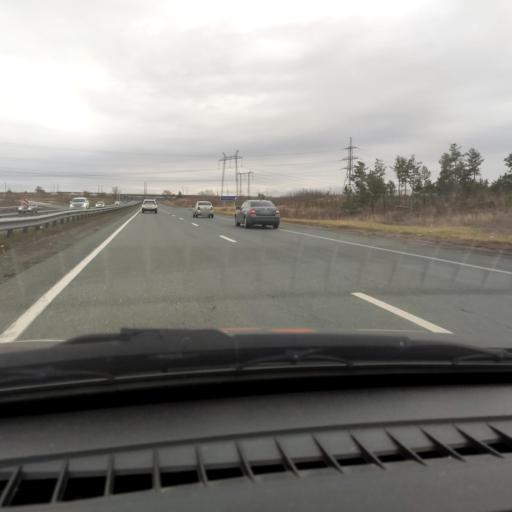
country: RU
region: Samara
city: Zhigulevsk
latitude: 53.5217
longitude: 49.5301
